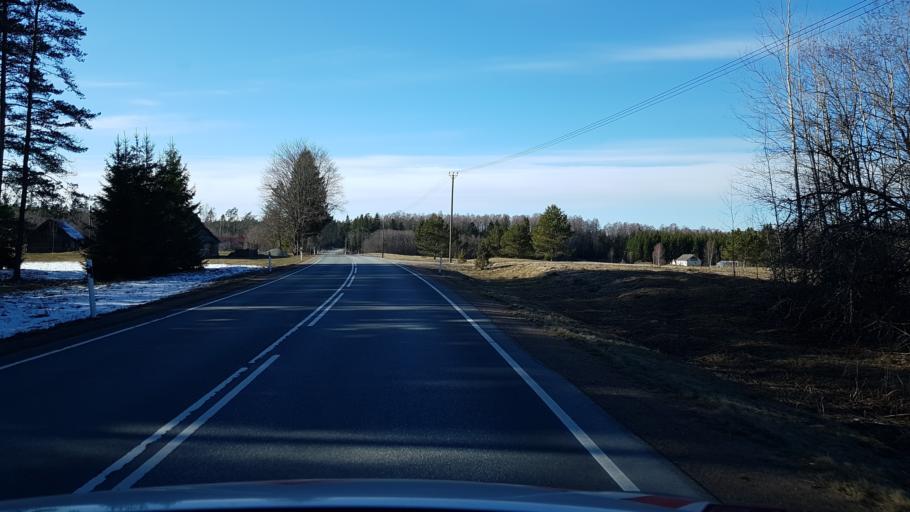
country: EE
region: Laeaene-Virumaa
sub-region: Tapa vald
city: Tapa
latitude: 59.4134
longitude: 25.9999
